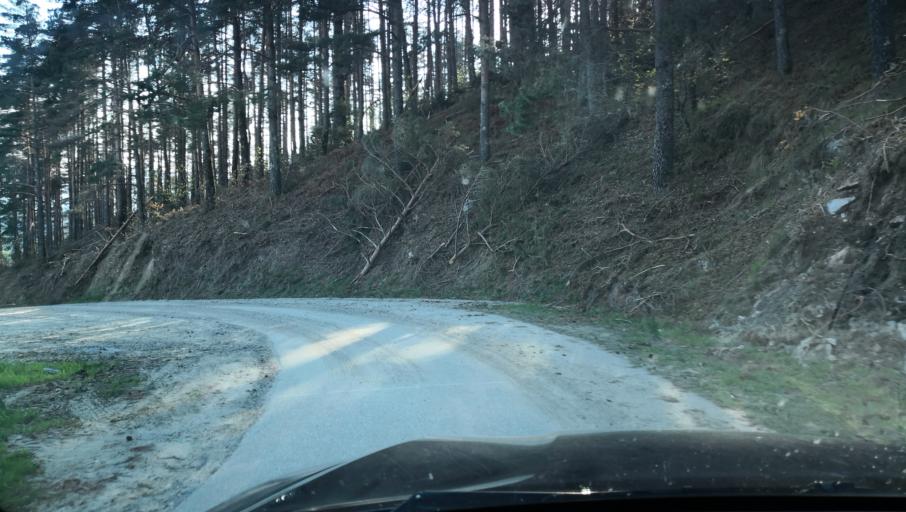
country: PT
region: Vila Real
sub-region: Vila Real
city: Vila Real
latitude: 41.3188
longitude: -7.8621
